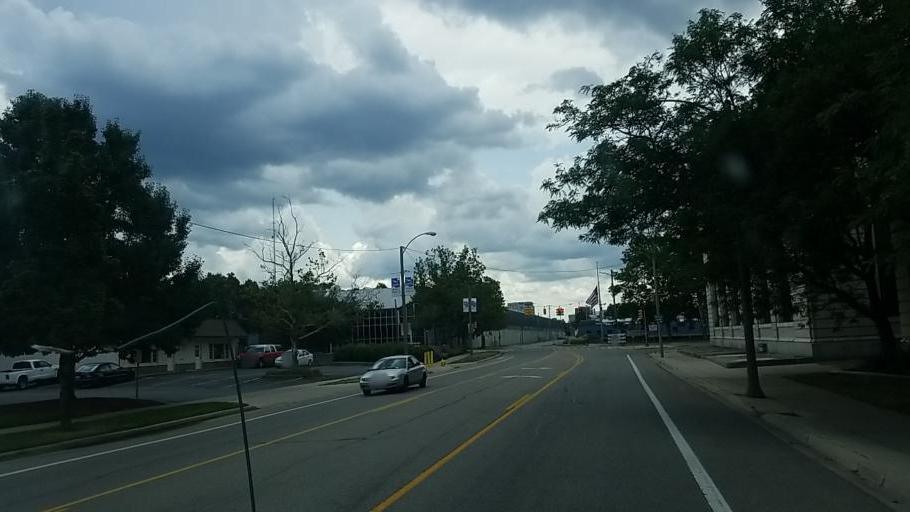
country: US
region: Michigan
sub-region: Kent County
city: Grand Rapids
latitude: 42.9831
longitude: -85.6708
